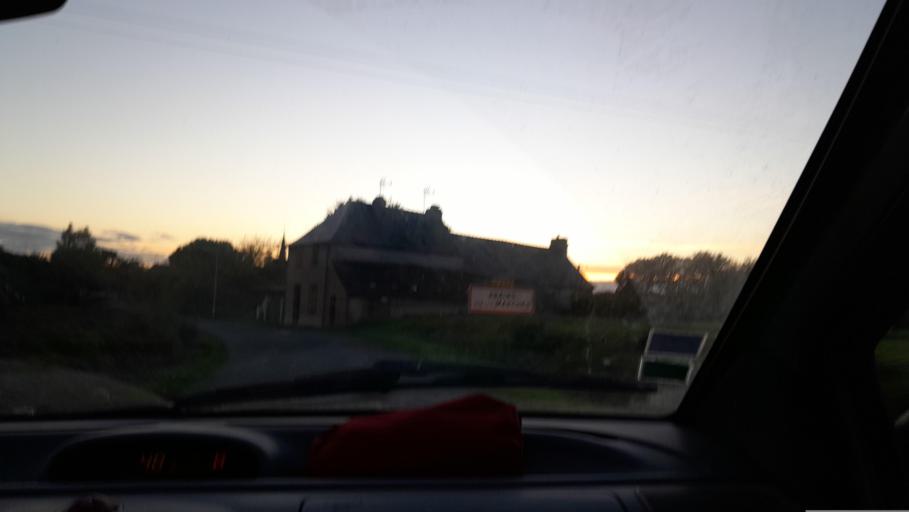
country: FR
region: Brittany
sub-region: Departement d'Ille-et-Vilaine
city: Rannee
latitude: 47.8883
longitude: -1.1790
